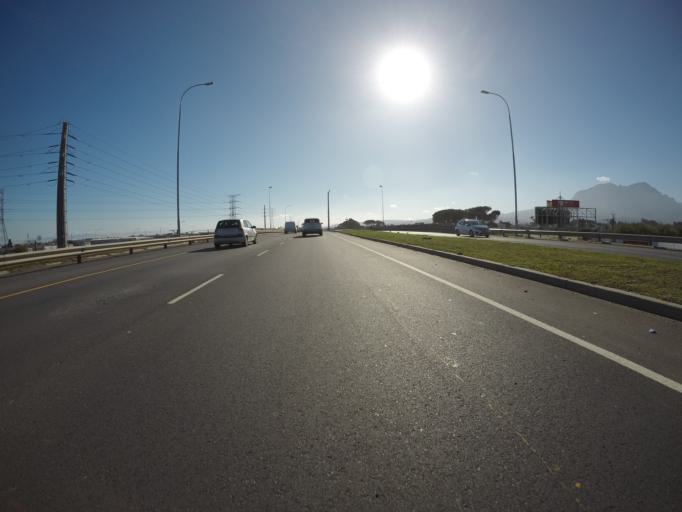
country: ZA
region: Western Cape
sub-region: Cape Winelands District Municipality
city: Stellenbosch
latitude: -34.1008
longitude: 18.8515
